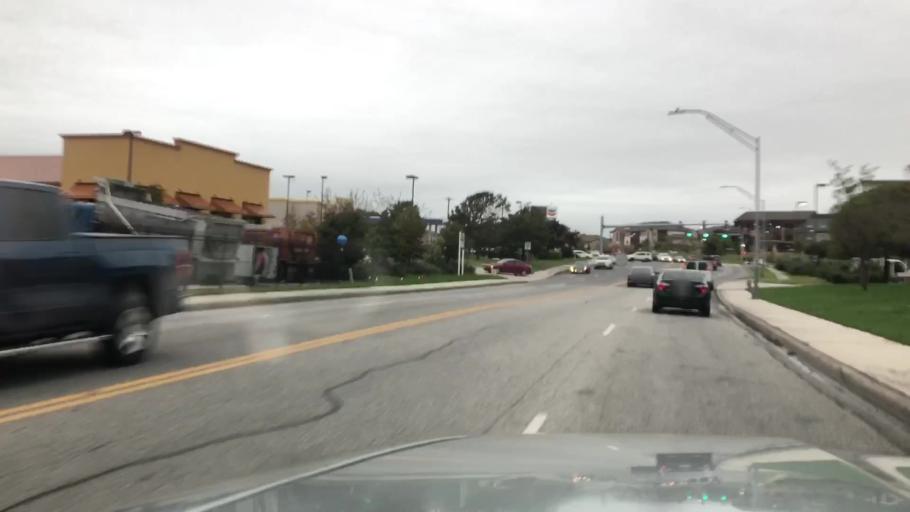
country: US
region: Texas
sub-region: Bexar County
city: Leon Valley
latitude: 29.5180
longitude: -98.6033
